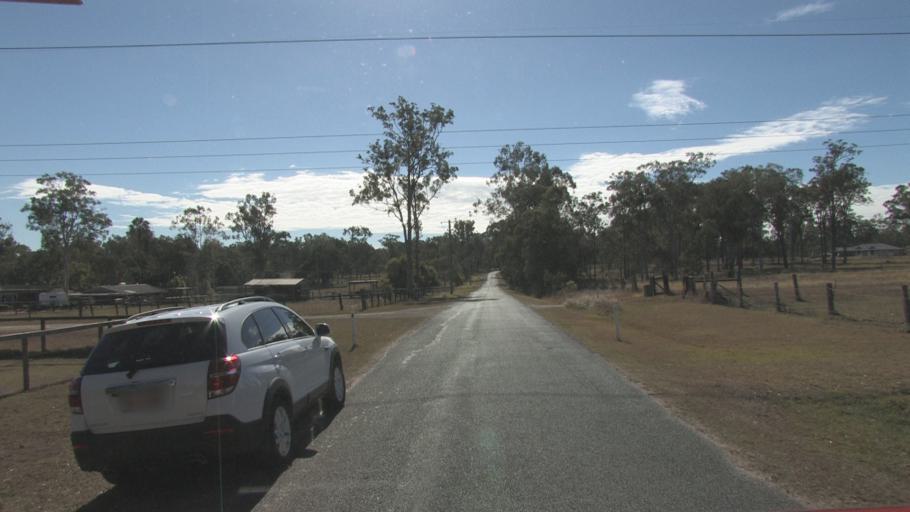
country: AU
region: Queensland
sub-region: Logan
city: Chambers Flat
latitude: -27.7891
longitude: 153.0669
